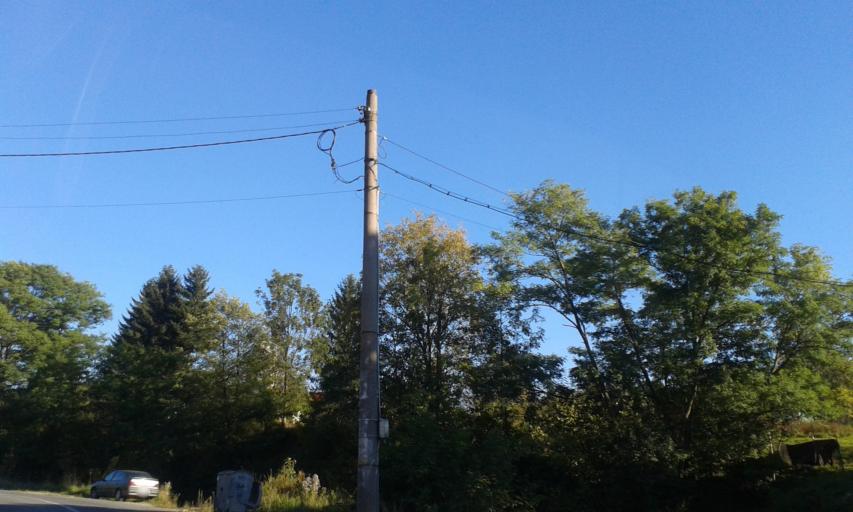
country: RO
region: Hunedoara
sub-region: Municipiul Petrosani
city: Petrosani
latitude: 45.4272
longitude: 23.3908
